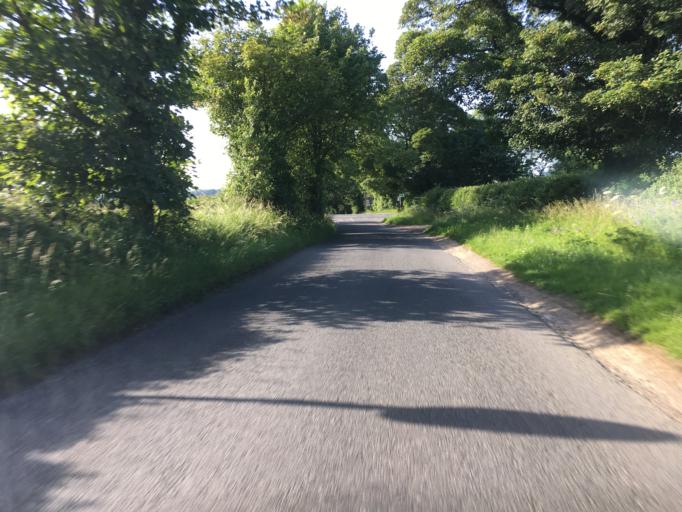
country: GB
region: England
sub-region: Oxfordshire
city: Burford
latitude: 51.8064
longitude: -1.7010
